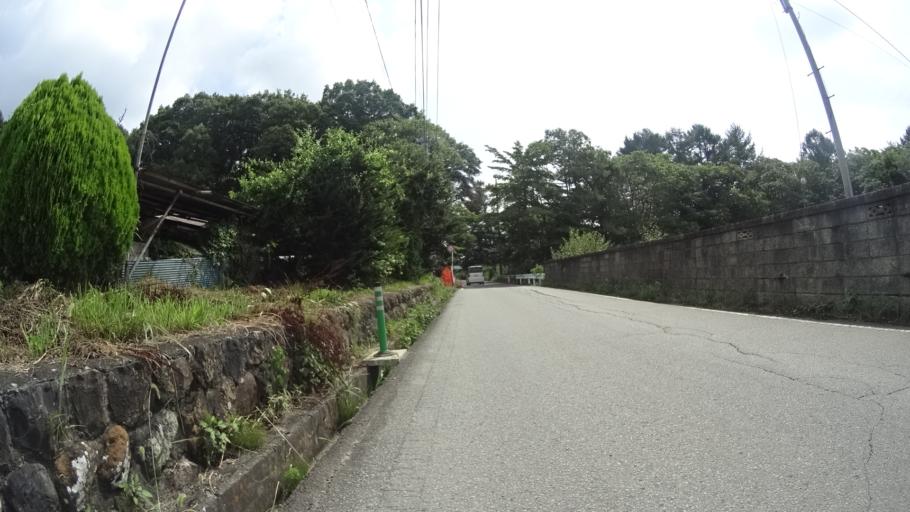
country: JP
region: Yamanashi
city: Nirasaki
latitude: 35.8740
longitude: 138.3442
